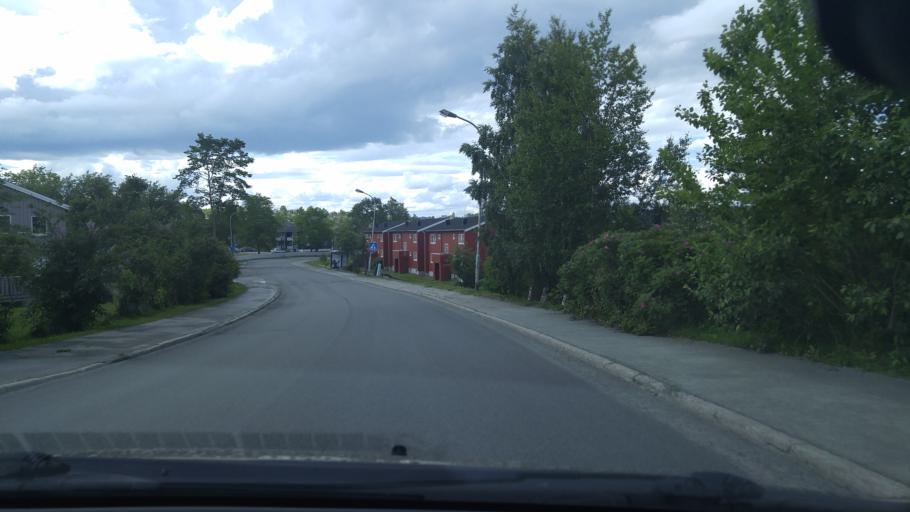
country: NO
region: Sor-Trondelag
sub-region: Trondheim
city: Trondheim
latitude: 63.4058
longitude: 10.4340
